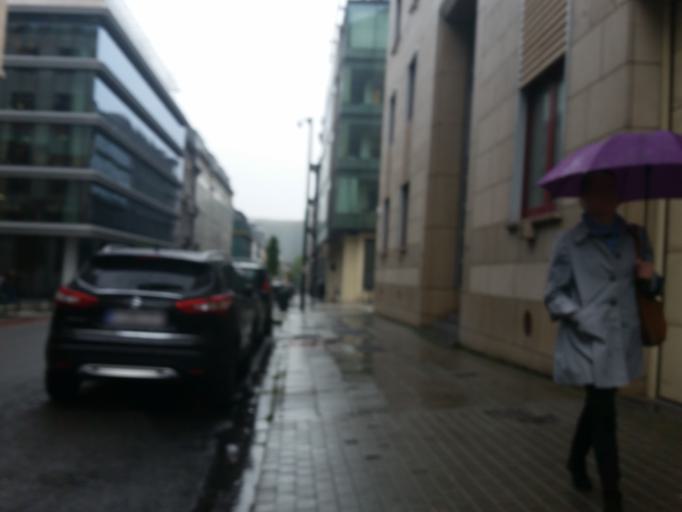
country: BE
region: Brussels Capital
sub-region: Bruxelles-Capitale
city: Brussels
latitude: 50.8459
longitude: 4.3719
